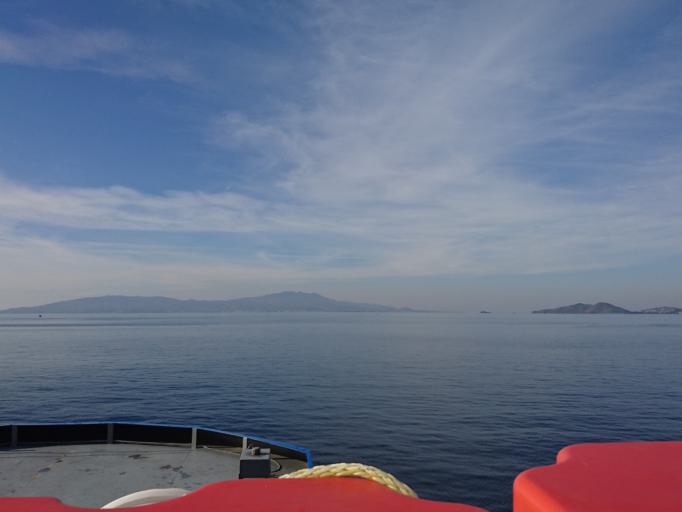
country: TR
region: Mugla
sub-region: Bodrum
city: Bodrum
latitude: 36.9912
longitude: 27.3932
